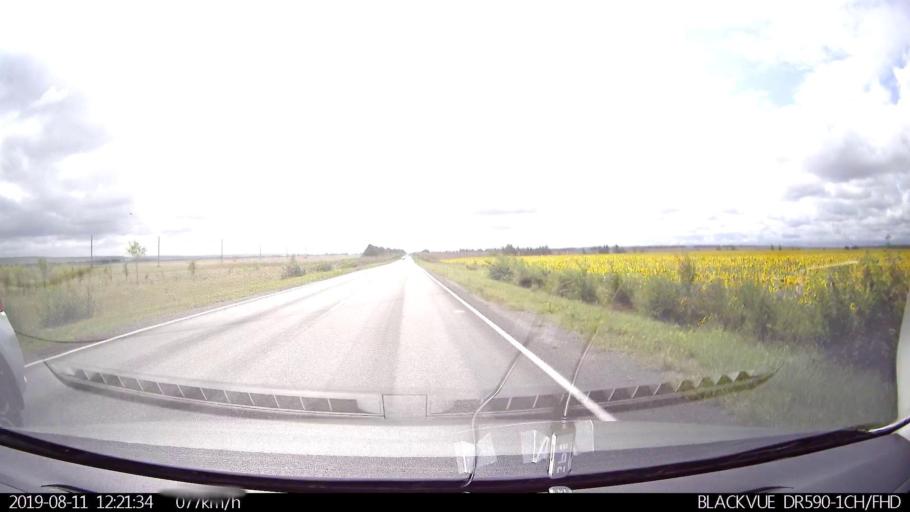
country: RU
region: Ulyanovsk
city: Ignatovka
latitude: 53.9195
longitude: 47.9574
